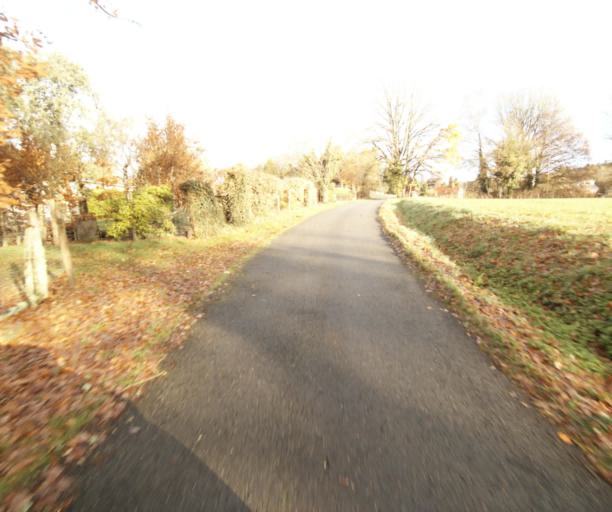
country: FR
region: Limousin
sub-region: Departement de la Correze
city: Saint-Mexant
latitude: 45.2644
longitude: 1.6293
